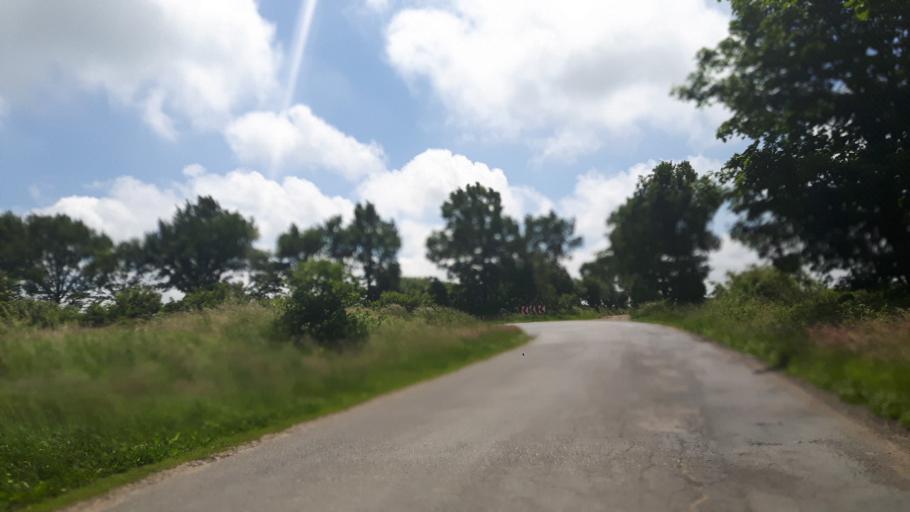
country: PL
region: West Pomeranian Voivodeship
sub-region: Powiat slawienski
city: Slawno
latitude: 54.5066
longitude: 16.6237
